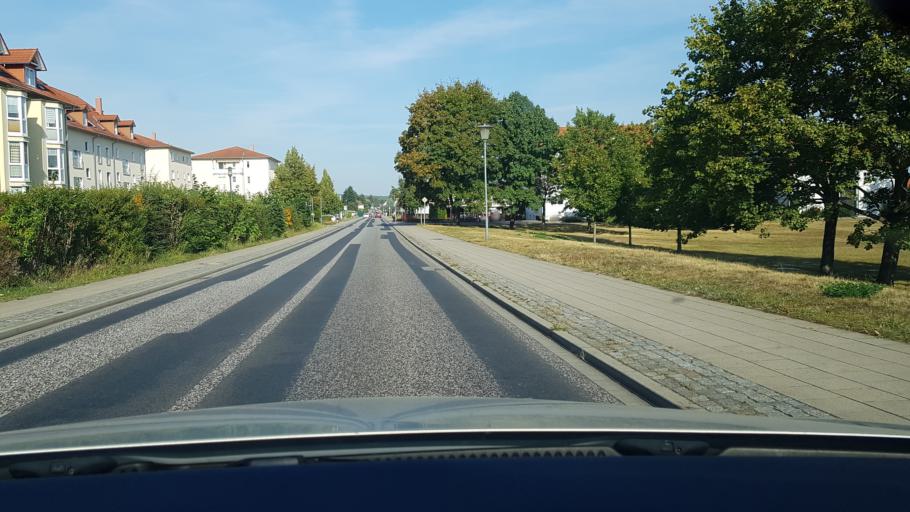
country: DE
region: Brandenburg
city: Eisenhuettenstadt
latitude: 52.1471
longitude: 14.6175
